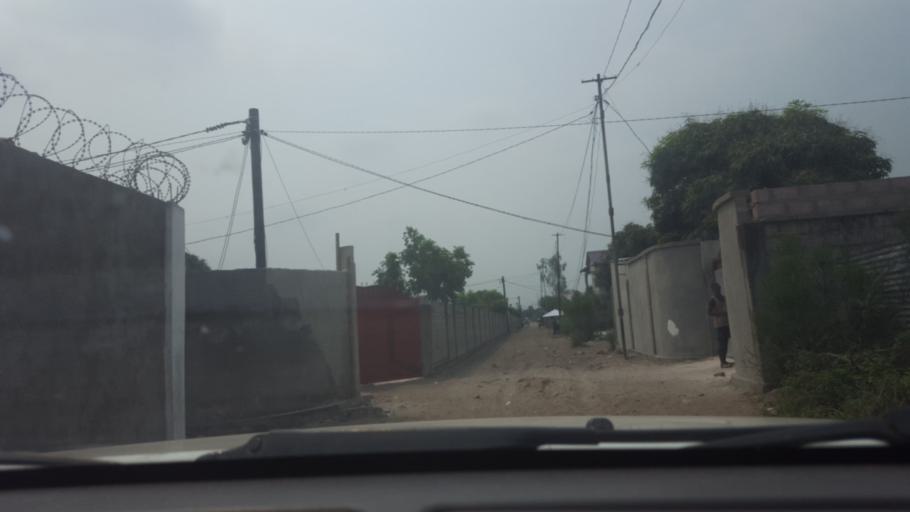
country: CD
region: Kinshasa
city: Masina
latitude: -4.3546
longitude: 15.5079
